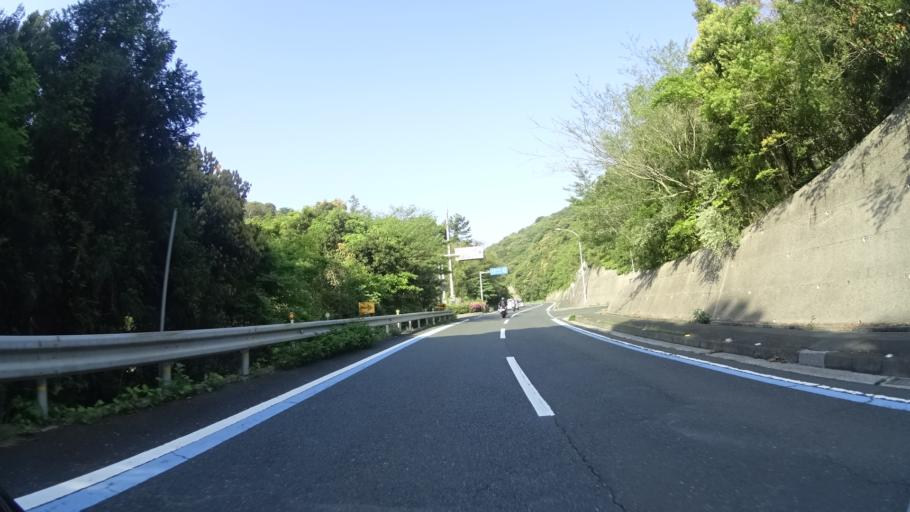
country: JP
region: Ehime
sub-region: Nishiuwa-gun
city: Ikata-cho
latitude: 33.4363
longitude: 132.2341
